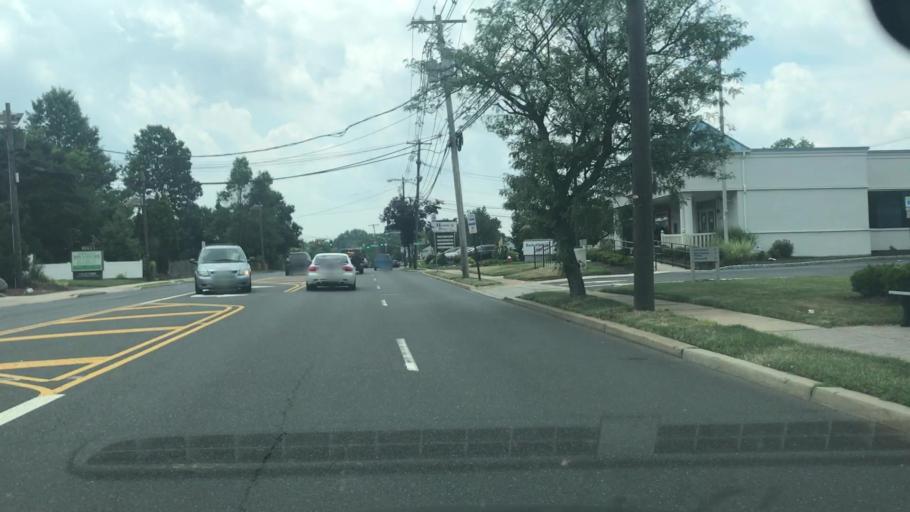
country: US
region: New Jersey
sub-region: Union County
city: Clark
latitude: 40.6274
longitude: -74.3155
